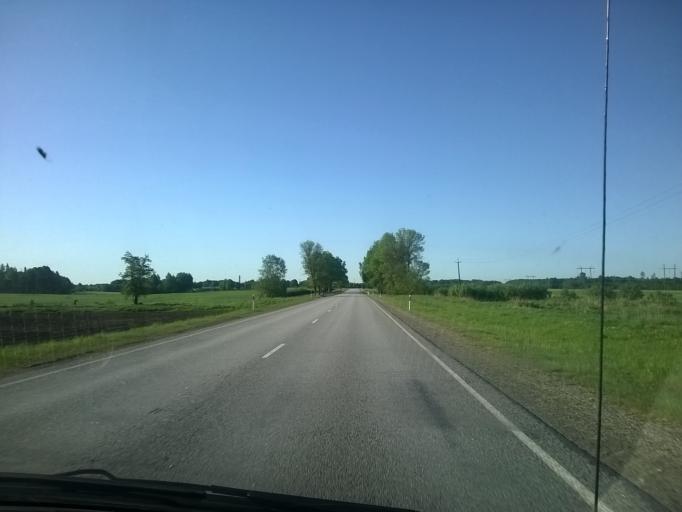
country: EE
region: Valgamaa
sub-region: Valga linn
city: Valga
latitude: 57.9388
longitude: 26.1690
